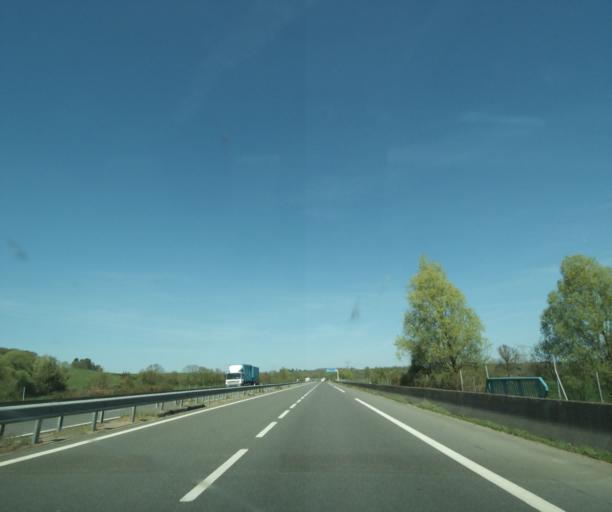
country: FR
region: Bourgogne
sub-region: Departement de la Nievre
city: Pougues-les-Eaux
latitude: 47.0687
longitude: 3.1284
